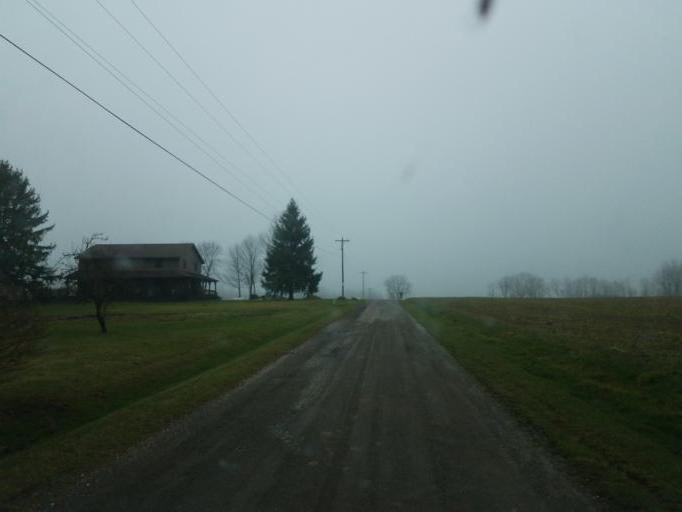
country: US
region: Ohio
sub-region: Richland County
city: Lexington
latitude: 40.6736
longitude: -82.6550
